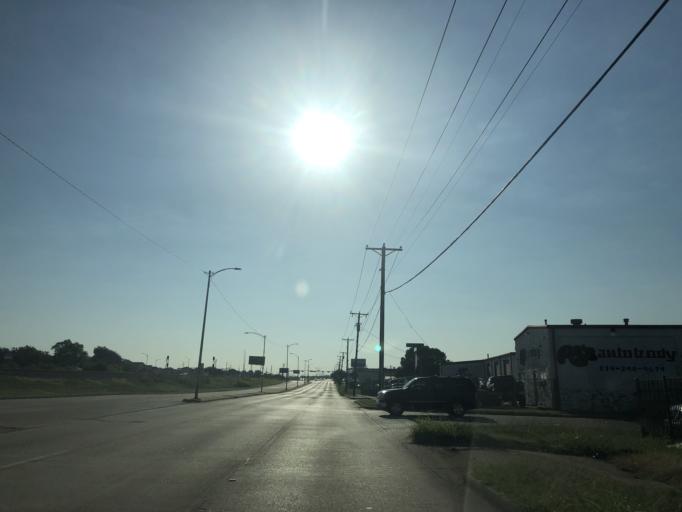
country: US
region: Texas
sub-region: Dallas County
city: Grand Prairie
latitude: 32.7394
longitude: -97.0331
